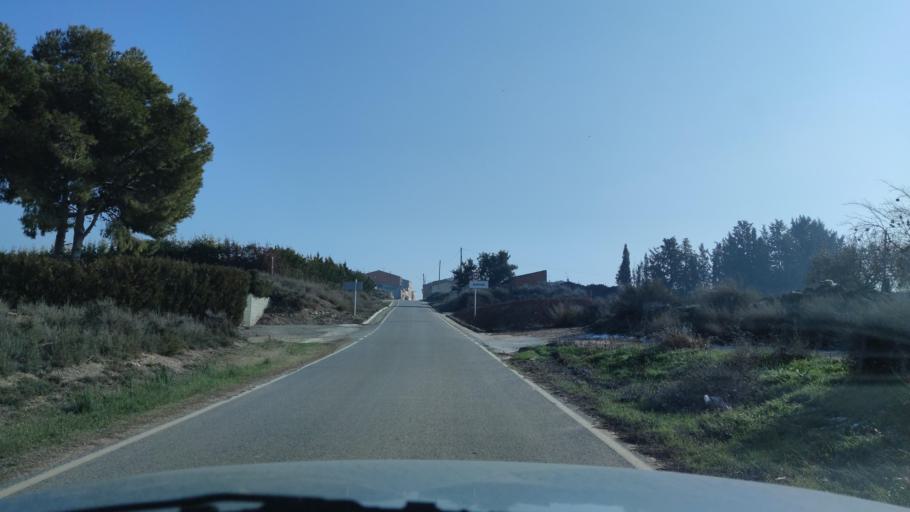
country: ES
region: Catalonia
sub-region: Provincia de Lleida
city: Sunyer
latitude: 41.5242
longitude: 0.5889
